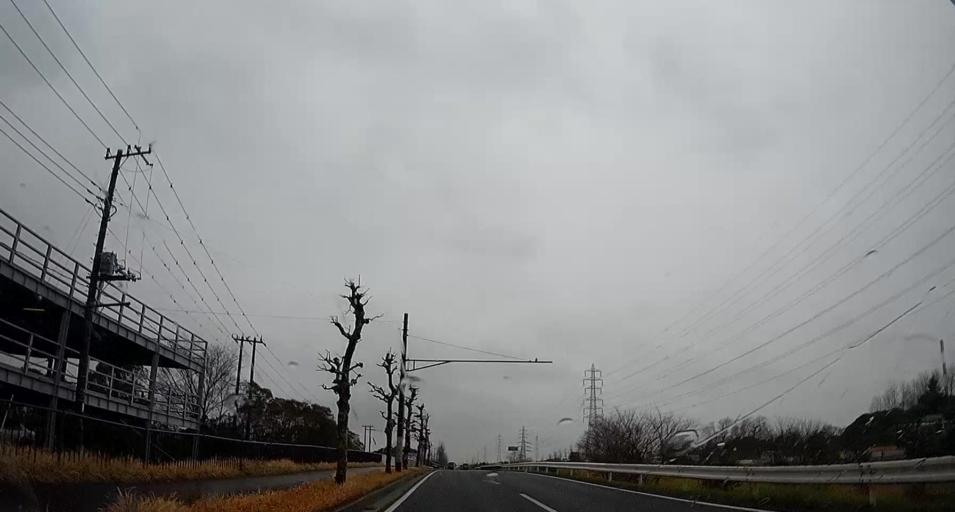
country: JP
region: Chiba
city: Ichihara
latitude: 35.5064
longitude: 140.0531
